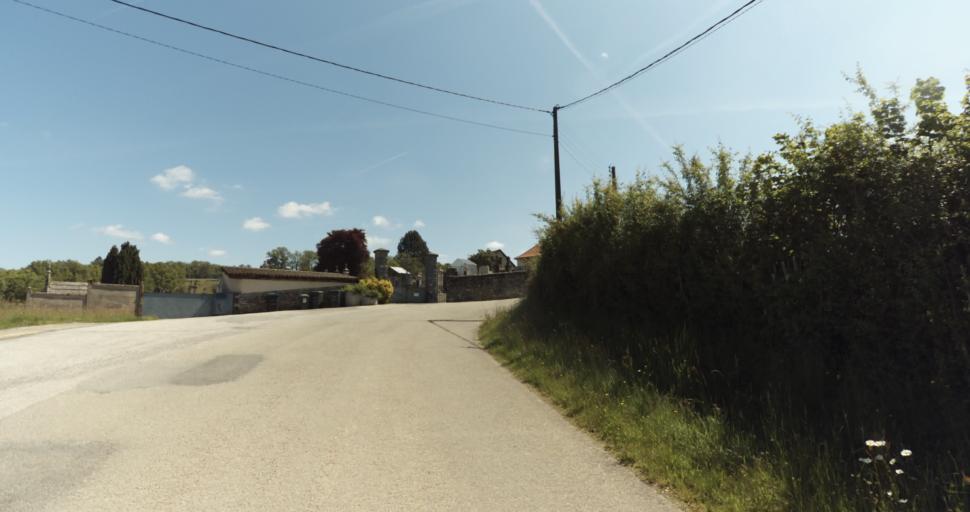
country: FR
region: Limousin
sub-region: Departement de la Haute-Vienne
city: Le Vigen
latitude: 45.7504
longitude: 1.2919
